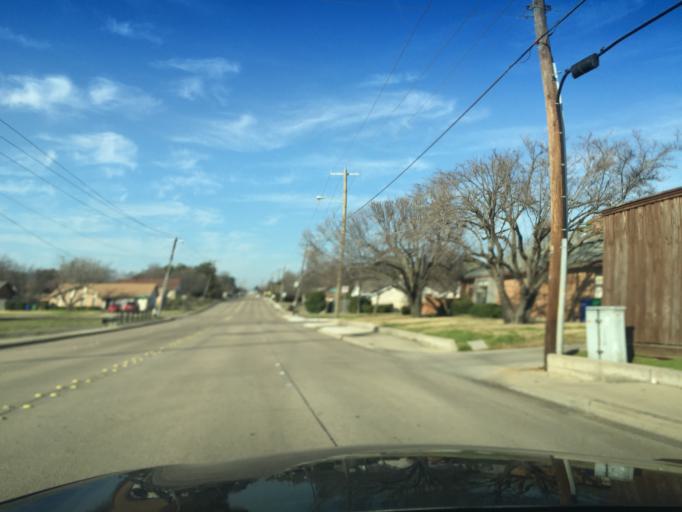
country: US
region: Texas
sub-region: Dallas County
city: Carrollton
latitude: 32.9790
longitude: -96.8841
